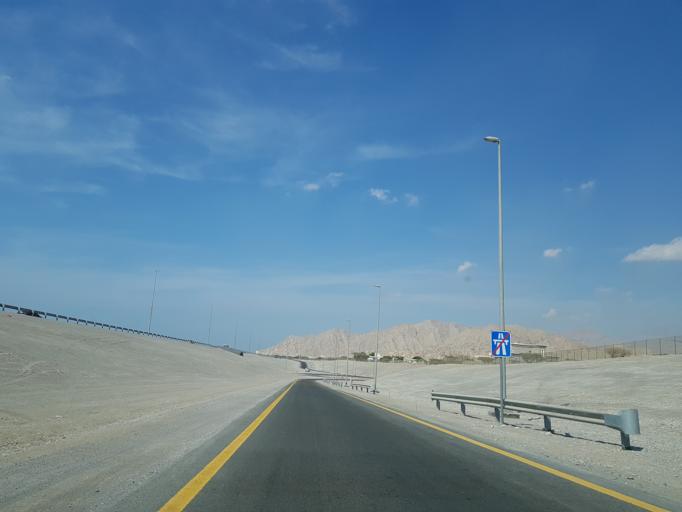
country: AE
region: Ra's al Khaymah
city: Ras al-Khaimah
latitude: 25.7968
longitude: 56.0314
